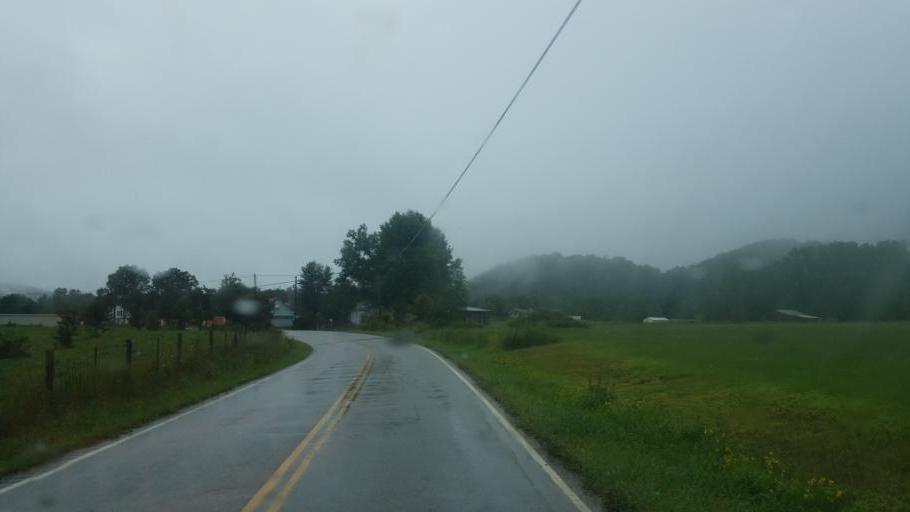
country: US
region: Kentucky
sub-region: Greenup County
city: South Shore
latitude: 38.6854
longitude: -82.9188
